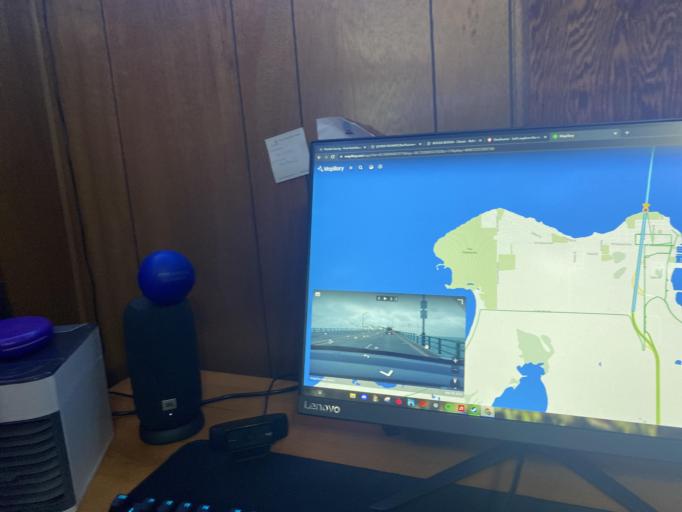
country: US
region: Michigan
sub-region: Mackinac County
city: Saint Ignace
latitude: 45.7846
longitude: -84.7302
